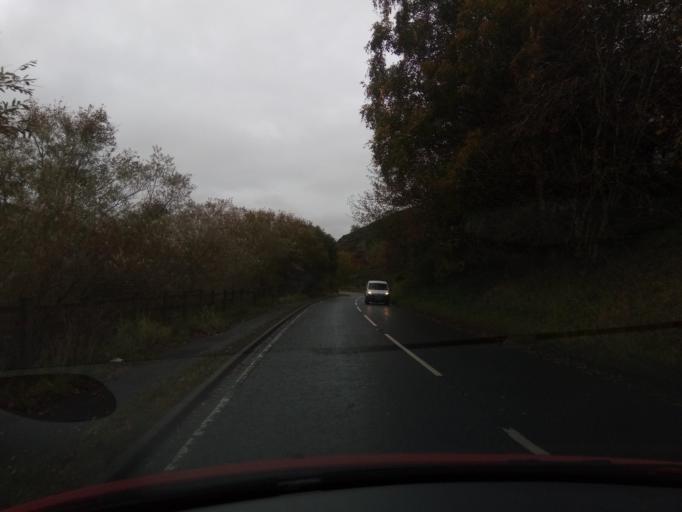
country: GB
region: Scotland
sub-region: The Scottish Borders
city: Galashiels
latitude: 55.6206
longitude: -2.8701
